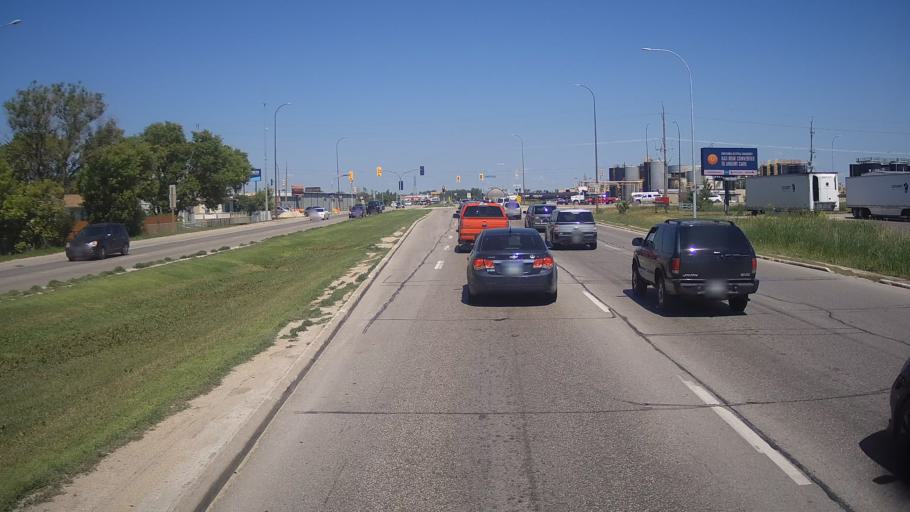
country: CA
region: Manitoba
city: Winnipeg
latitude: 49.8847
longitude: -97.0721
